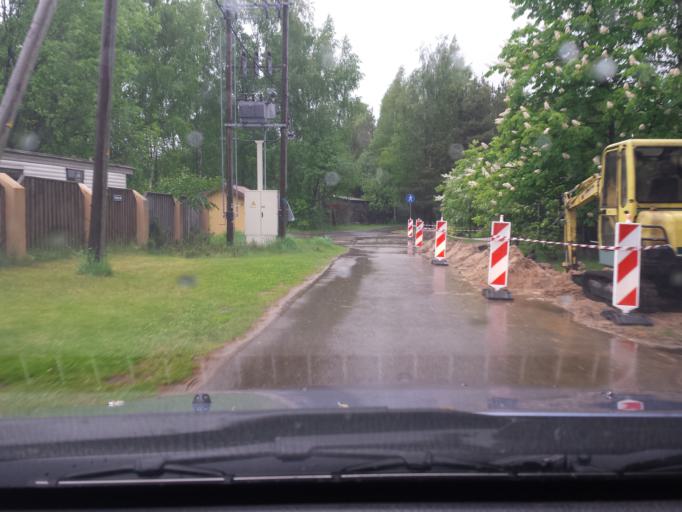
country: LV
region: Riga
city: Bolderaja
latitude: 57.0759
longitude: 24.0975
